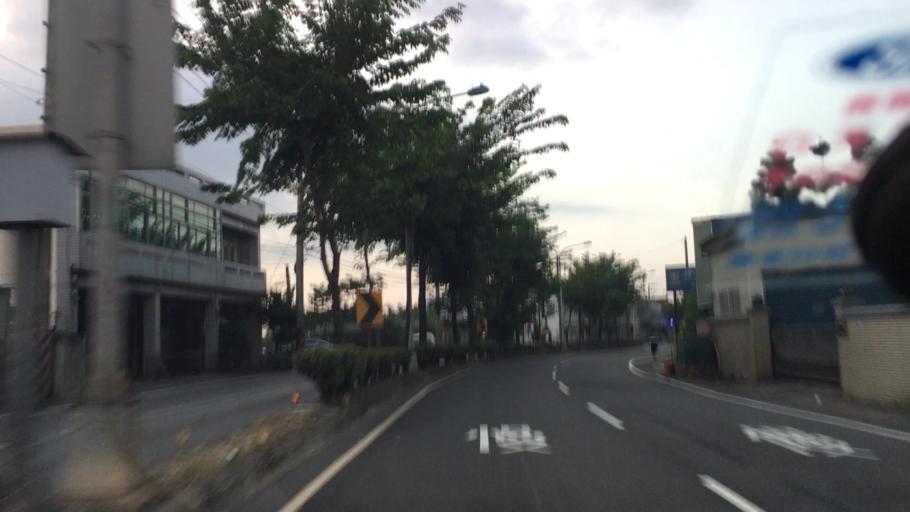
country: TW
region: Taiwan
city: Taoyuan City
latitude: 25.0571
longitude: 121.2684
